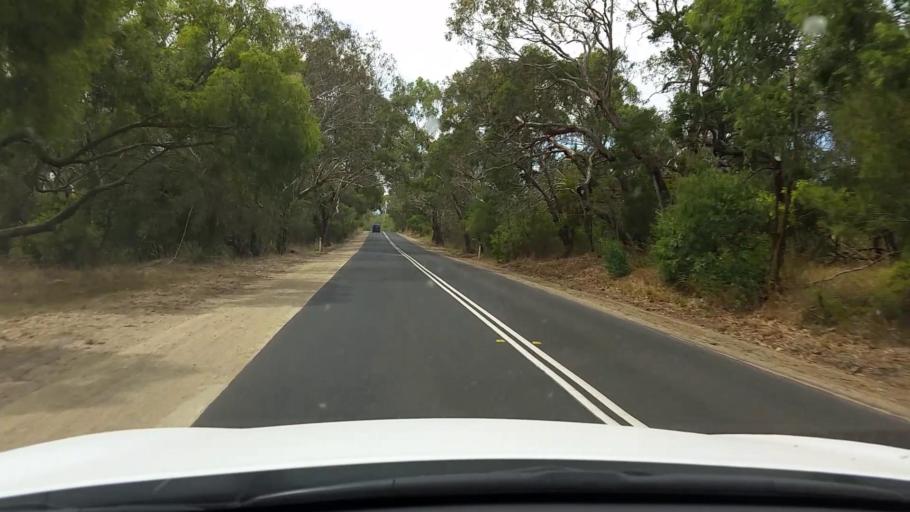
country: AU
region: Victoria
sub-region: Mornington Peninsula
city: Mount Martha
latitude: -38.3008
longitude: 145.0427
